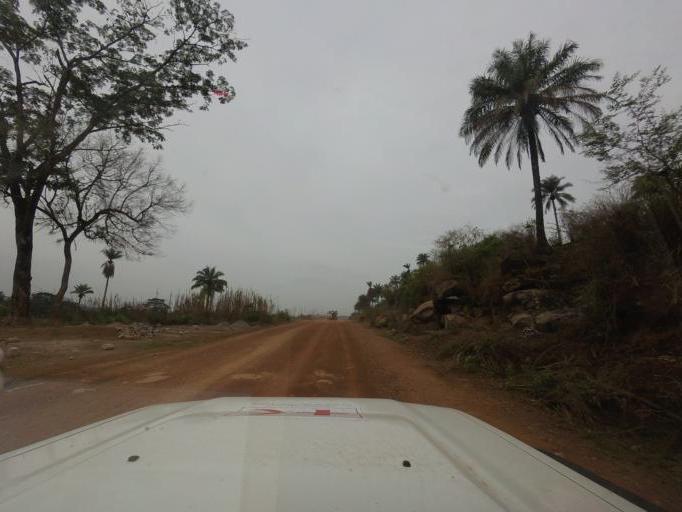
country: LR
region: Lofa
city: Voinjama
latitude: 8.3958
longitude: -9.7977
